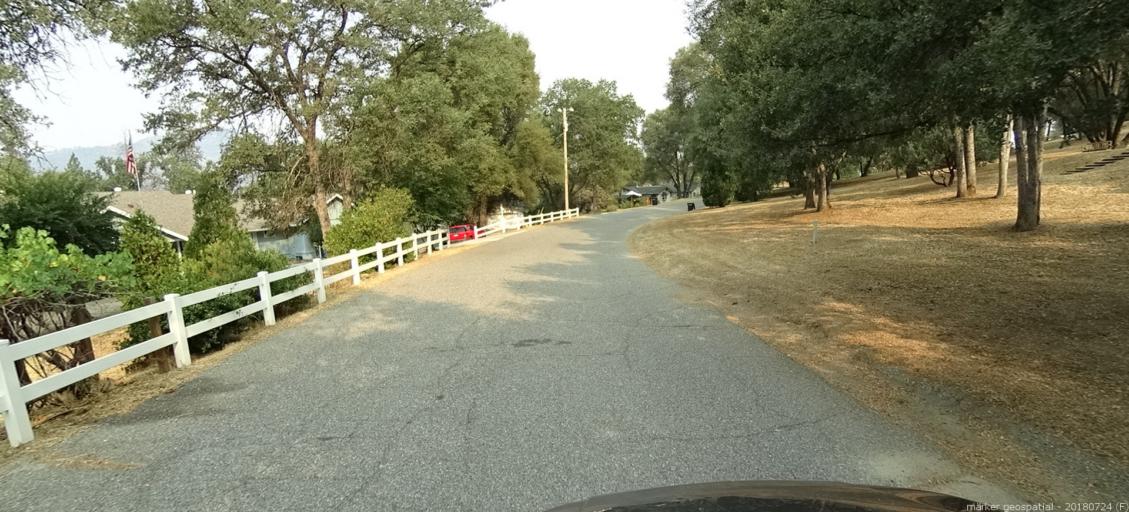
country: US
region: California
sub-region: Madera County
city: Oakhurst
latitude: 37.3195
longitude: -119.6342
